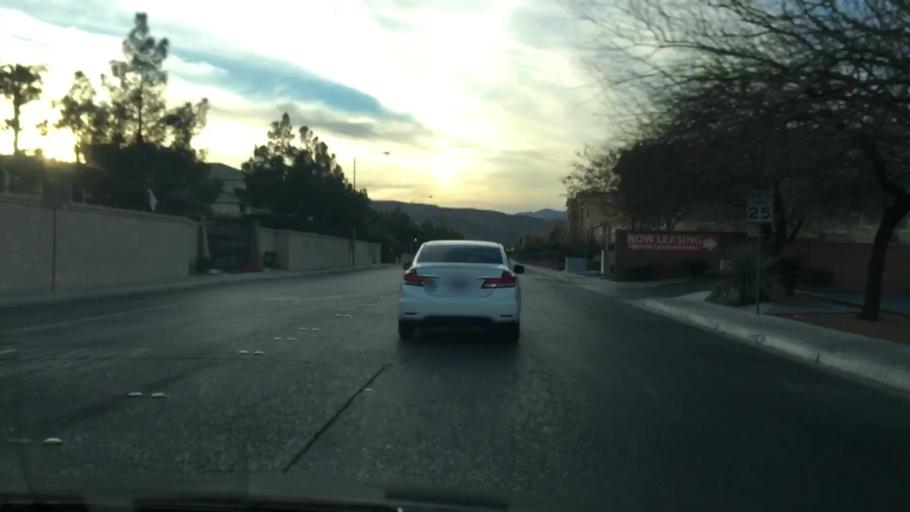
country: US
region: Nevada
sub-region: Clark County
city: Enterprise
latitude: 36.0593
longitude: -115.2799
